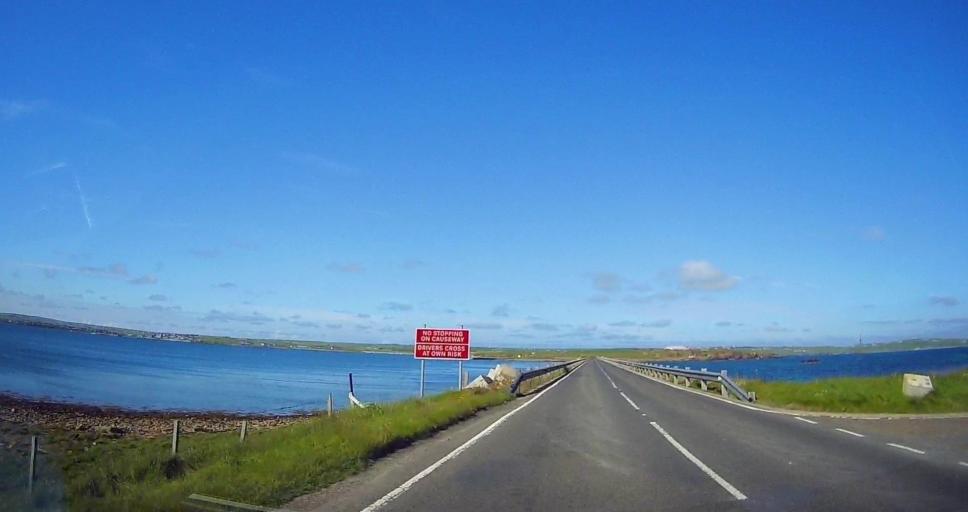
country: GB
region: Scotland
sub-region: Orkney Islands
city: Kirkwall
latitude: 58.8791
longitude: -2.9063
